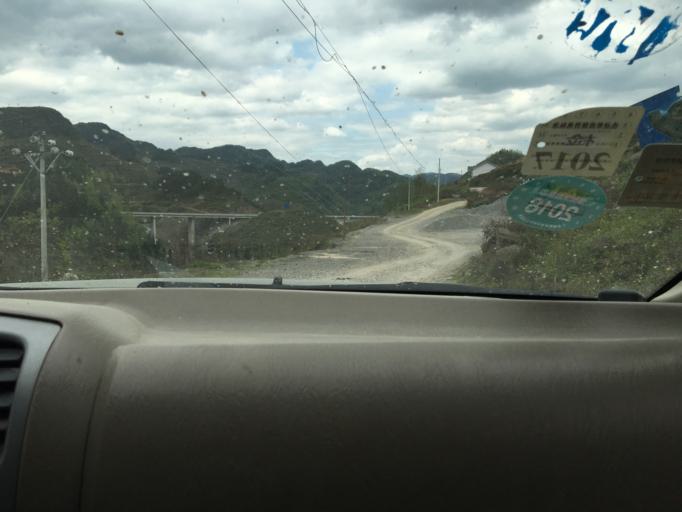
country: CN
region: Guizhou Sheng
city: Donghua
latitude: 28.0443
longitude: 108.0642
